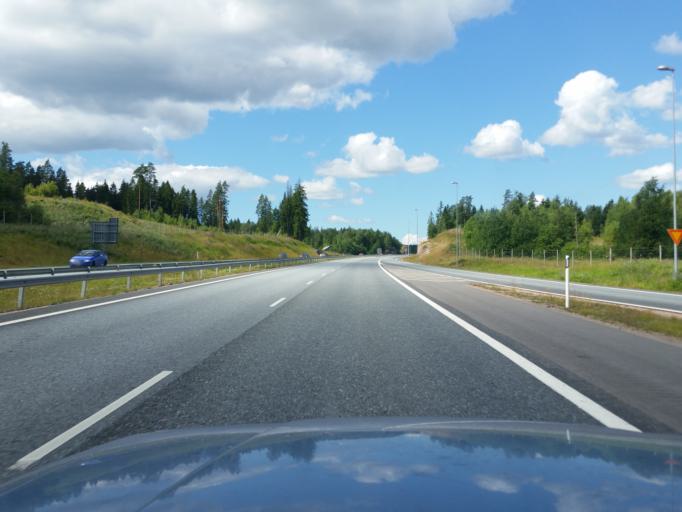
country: FI
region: Uusimaa
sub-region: Helsinki
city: Sammatti
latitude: 60.3789
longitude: 23.7982
